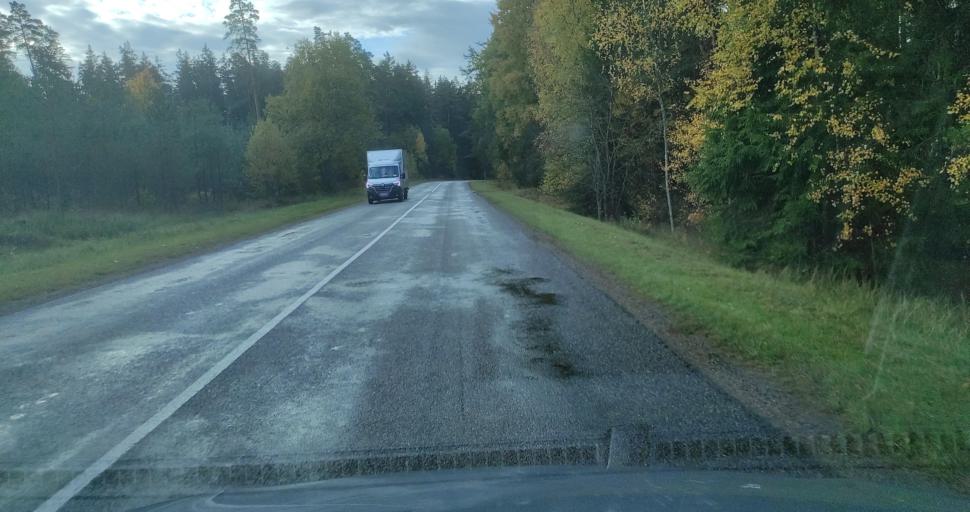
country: LV
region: Skrunda
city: Skrunda
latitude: 56.6363
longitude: 22.0058
